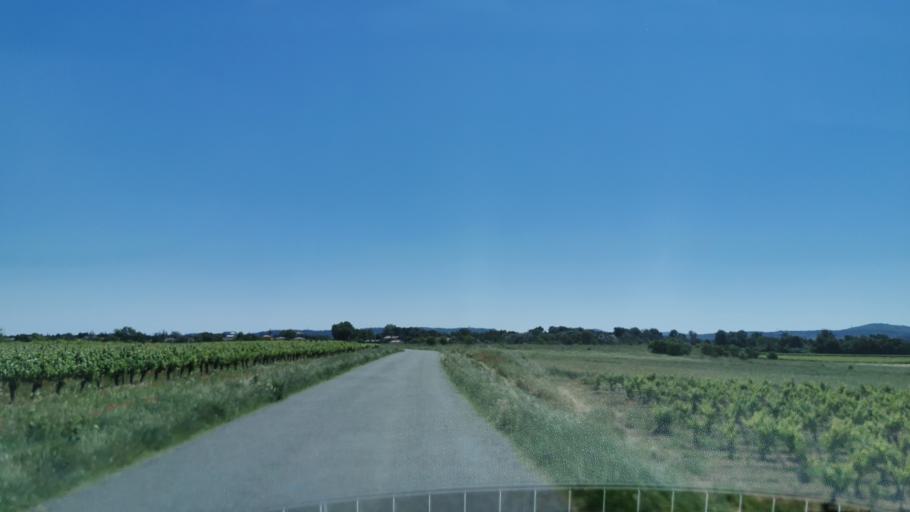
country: FR
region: Languedoc-Roussillon
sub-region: Departement de l'Aude
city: Ginestas
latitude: 43.2471
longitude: 2.8768
